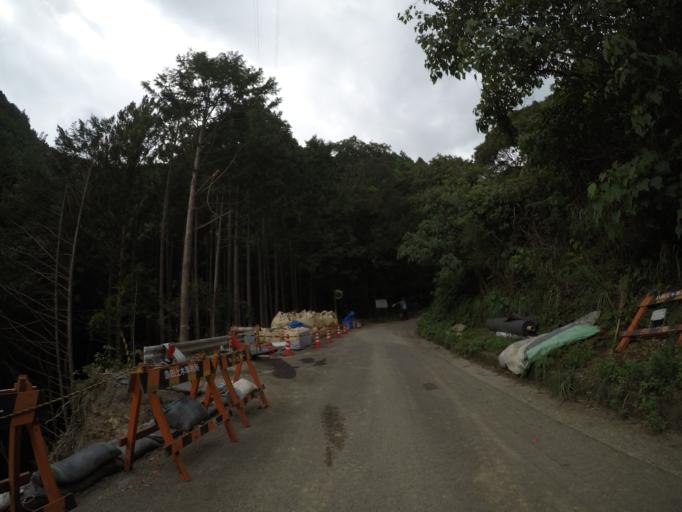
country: JP
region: Shizuoka
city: Shimada
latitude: 34.8820
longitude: 138.1720
